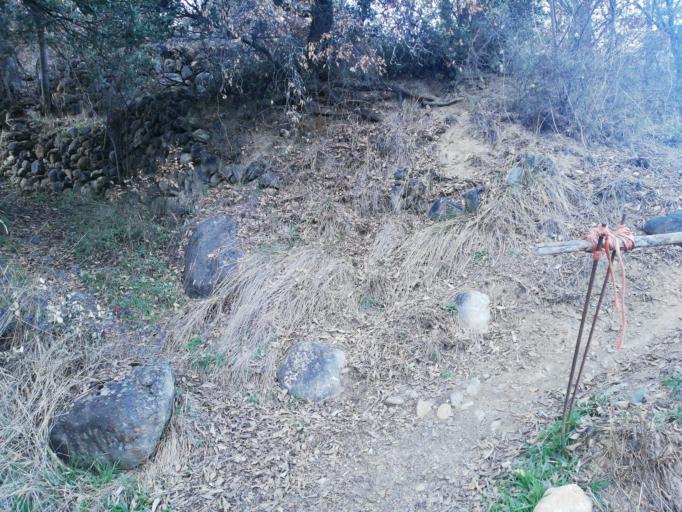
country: ES
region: Catalonia
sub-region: Provincia de Lleida
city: la Seu d'Urgell
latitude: 42.3588
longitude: 1.4381
